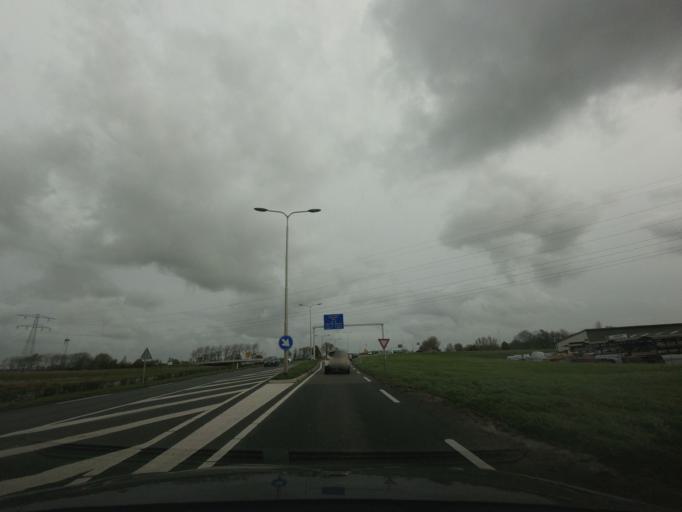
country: NL
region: North Holland
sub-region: Gemeente Heerhugowaard
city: Heerhugowaard
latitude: 52.7211
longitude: 4.8541
